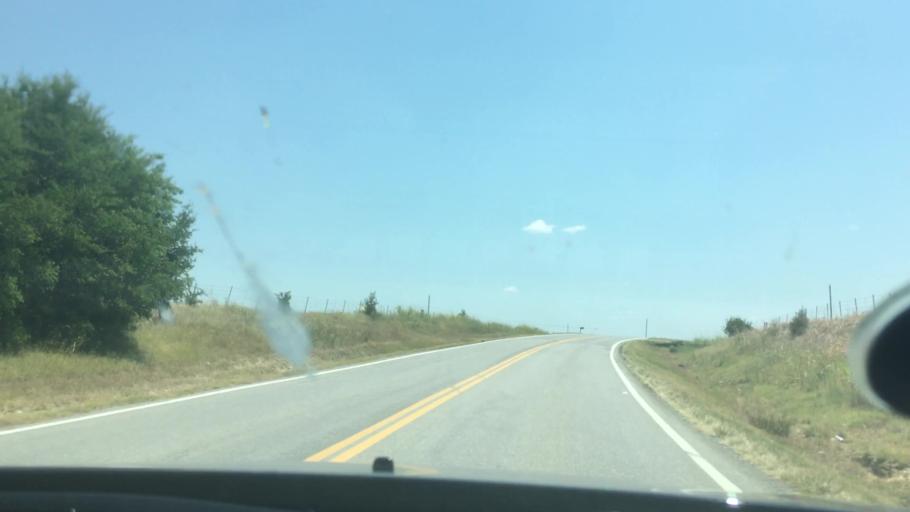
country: US
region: Oklahoma
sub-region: Bryan County
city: Durant
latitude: 34.1134
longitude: -96.3663
